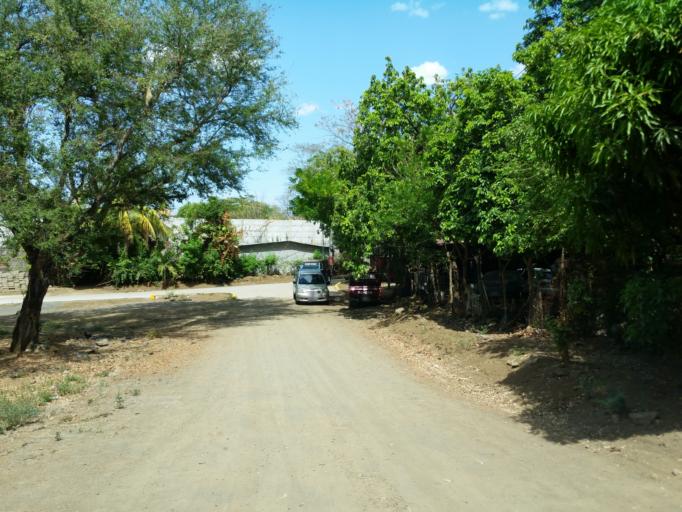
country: NI
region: Managua
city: Managua
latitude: 12.1007
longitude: -86.2522
